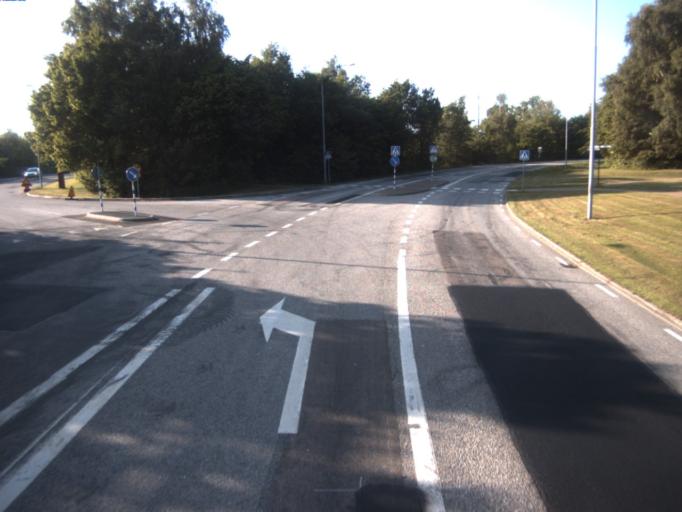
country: SE
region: Skane
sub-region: Helsingborg
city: Helsingborg
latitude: 56.0867
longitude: 12.6616
